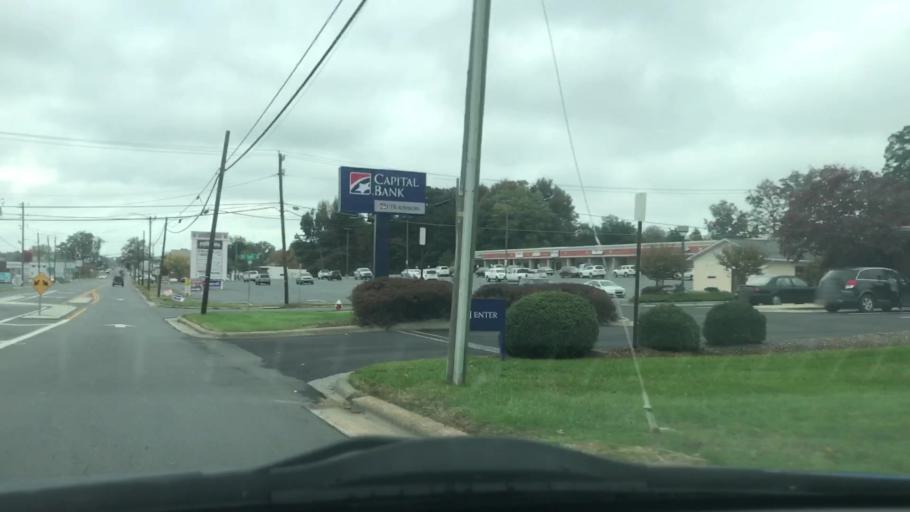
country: US
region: North Carolina
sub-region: Randolph County
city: Asheboro
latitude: 35.6919
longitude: -79.8157
